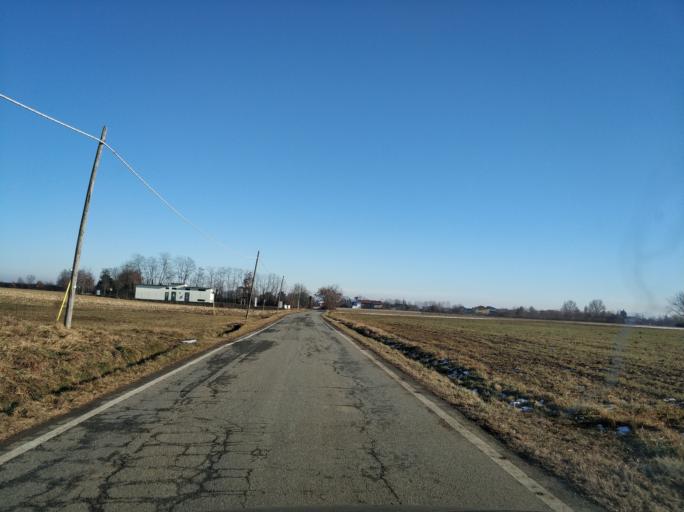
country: IT
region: Piedmont
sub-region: Provincia di Torino
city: San Carlo Canavese
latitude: 45.2421
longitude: 7.6285
